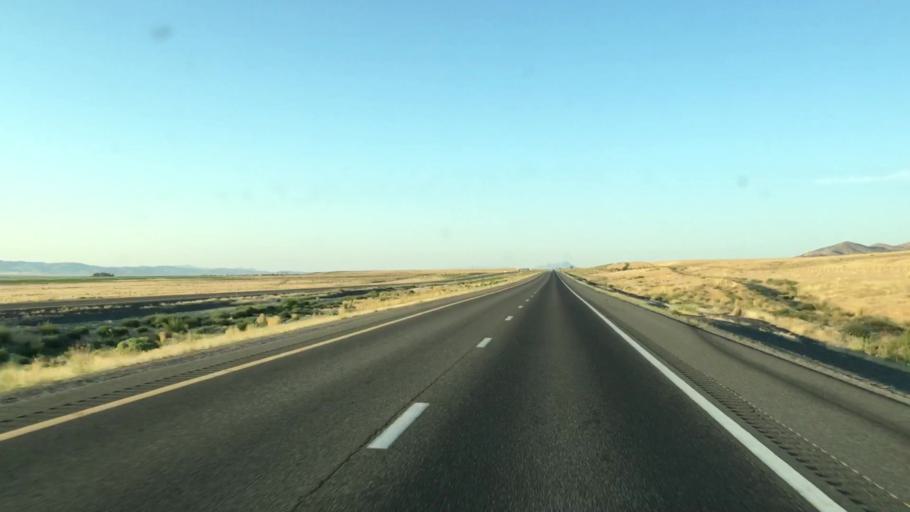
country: US
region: Nevada
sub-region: Humboldt County
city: Winnemucca
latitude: 40.7624
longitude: -118.0159
